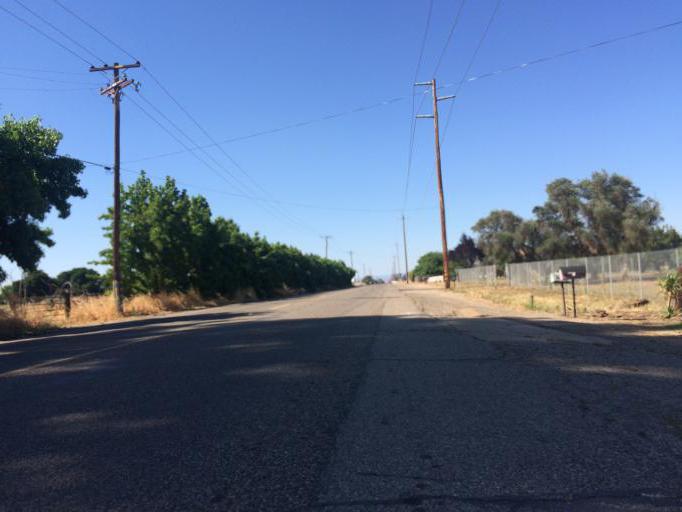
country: US
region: California
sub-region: Fresno County
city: Sanger
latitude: 36.7556
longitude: -119.6101
